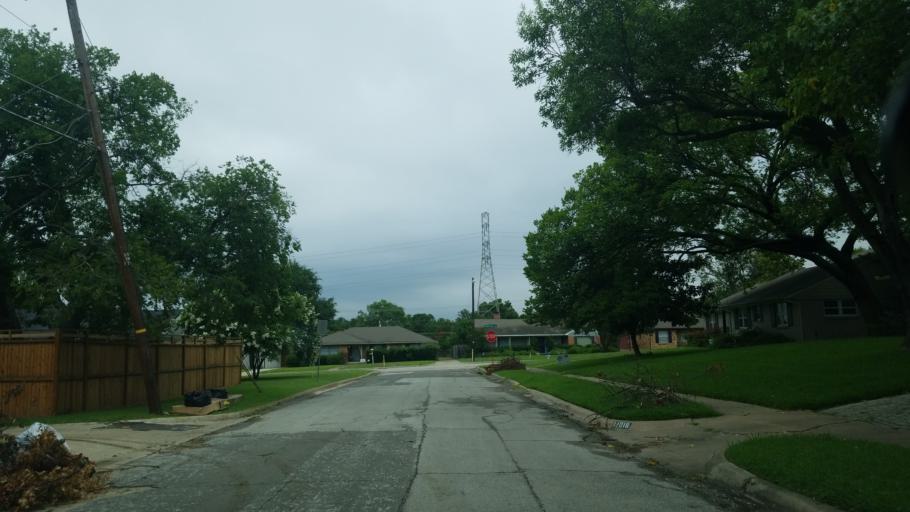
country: US
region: Texas
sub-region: Dallas County
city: Farmers Branch
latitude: 32.8985
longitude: -96.8574
